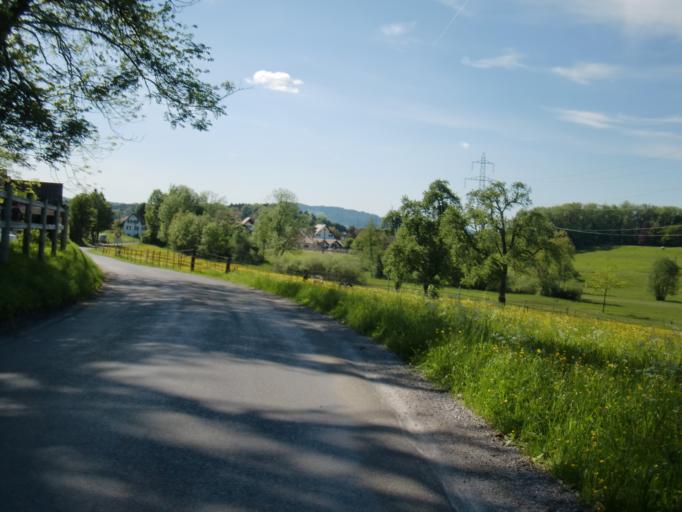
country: CH
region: Zurich
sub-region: Bezirk Meilen
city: Hombrechtikon
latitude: 47.2676
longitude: 8.7809
